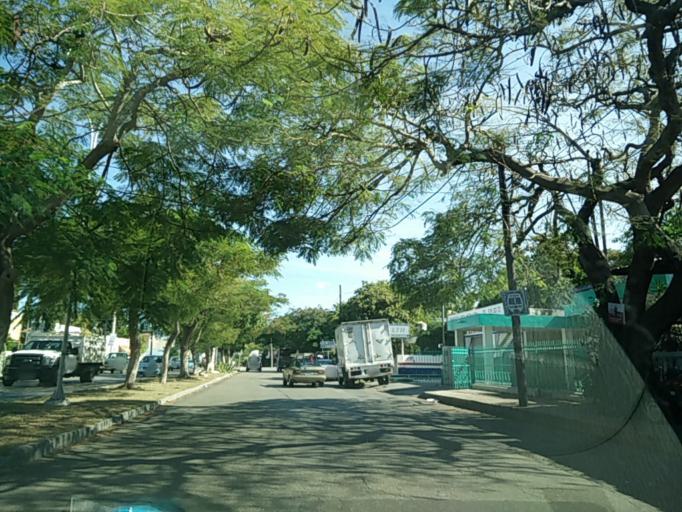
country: MX
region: Yucatan
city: Merida
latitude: 20.9970
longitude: -89.6053
